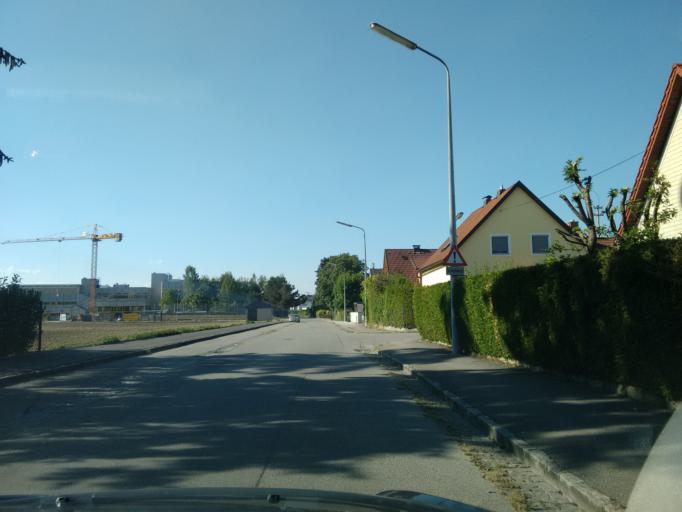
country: AT
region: Upper Austria
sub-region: Politischer Bezirk Linz-Land
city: Traun
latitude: 48.2262
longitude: 14.2489
